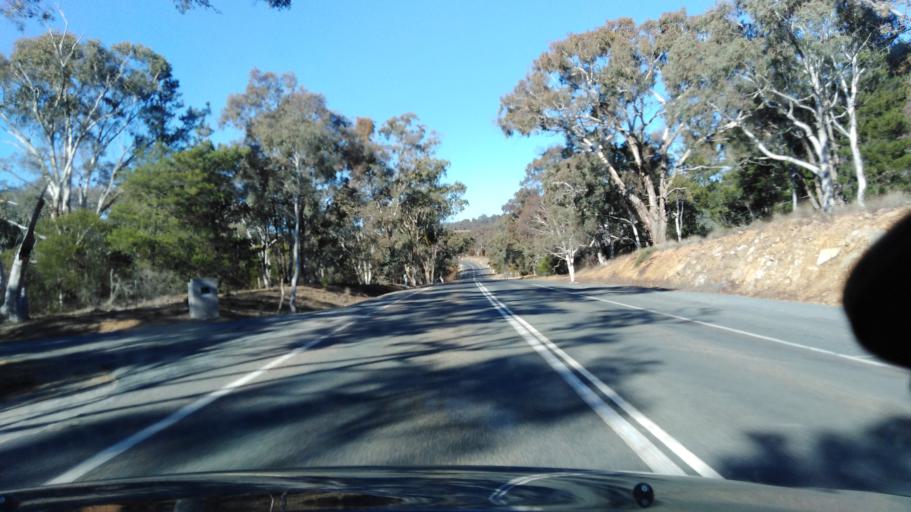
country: AU
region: New South Wales
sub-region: Yass Valley
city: Gundaroo
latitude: -35.1819
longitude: 149.2920
